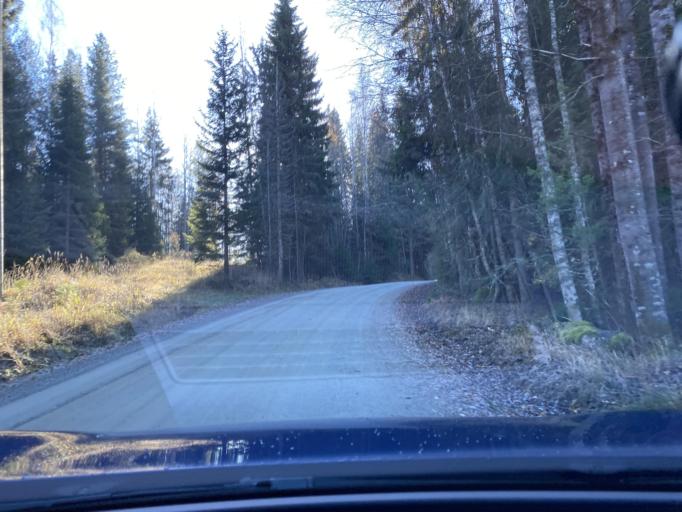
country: FI
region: Pirkanmaa
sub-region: Etelae-Pirkanmaa
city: Akaa
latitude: 61.0069
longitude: 23.9212
